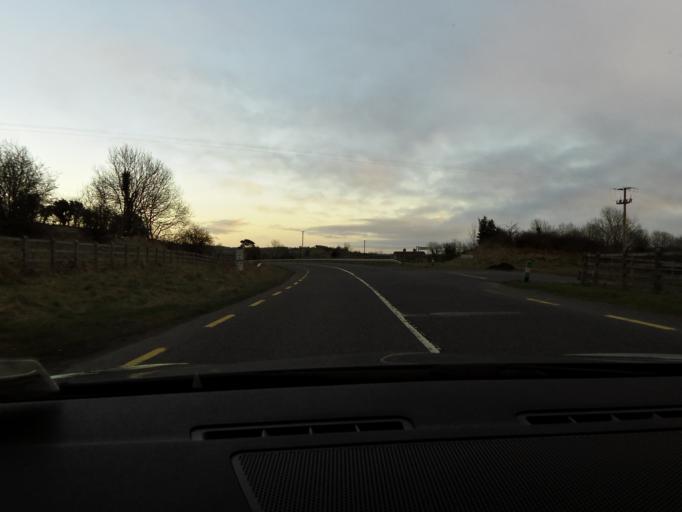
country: IE
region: Connaught
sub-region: Sligo
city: Ballymote
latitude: 53.9807
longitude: -8.4645
